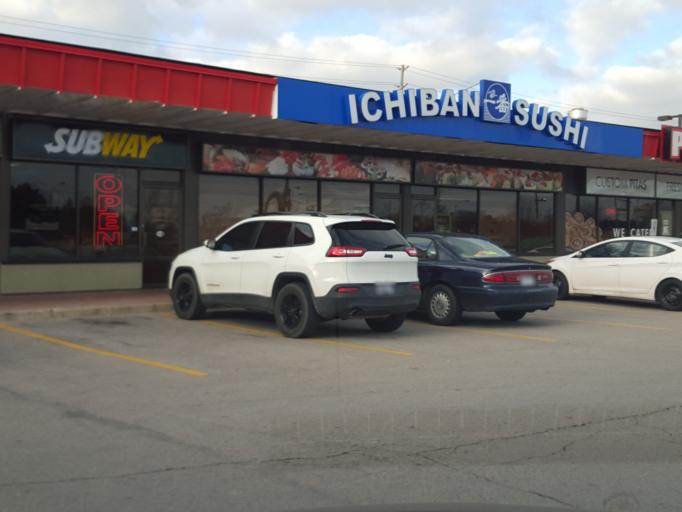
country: CA
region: Ontario
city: Burlington
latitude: 43.3546
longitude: -79.7864
